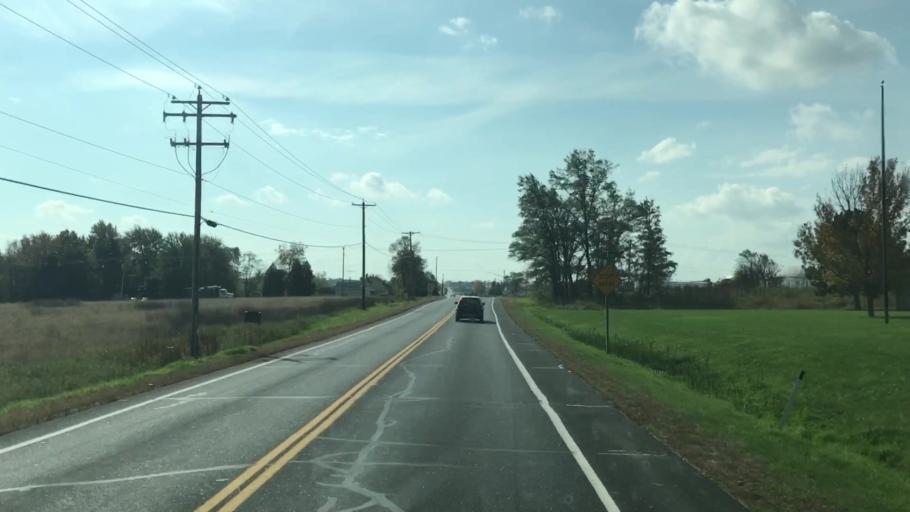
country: US
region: Wisconsin
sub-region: Ozaukee County
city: Mequon
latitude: 43.1940
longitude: -88.0436
